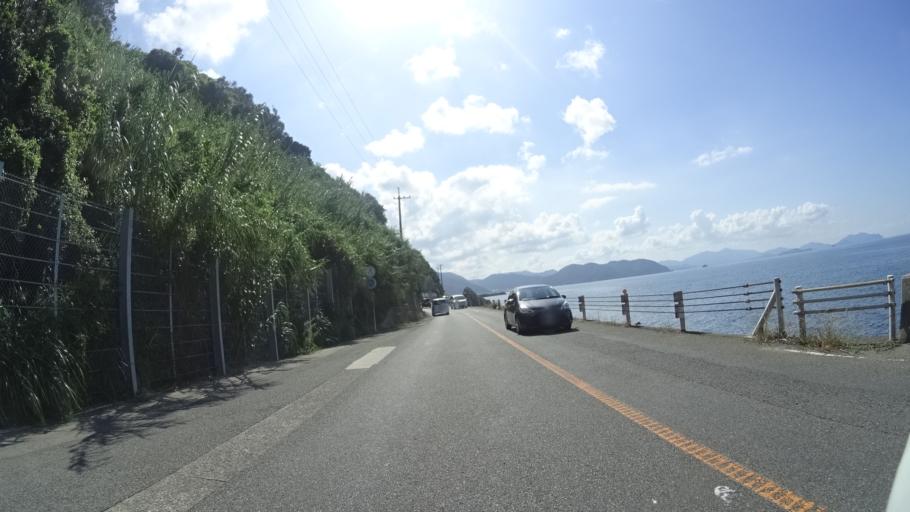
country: JP
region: Yamaguchi
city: Shimonoseki
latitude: 34.2534
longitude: 130.9023
